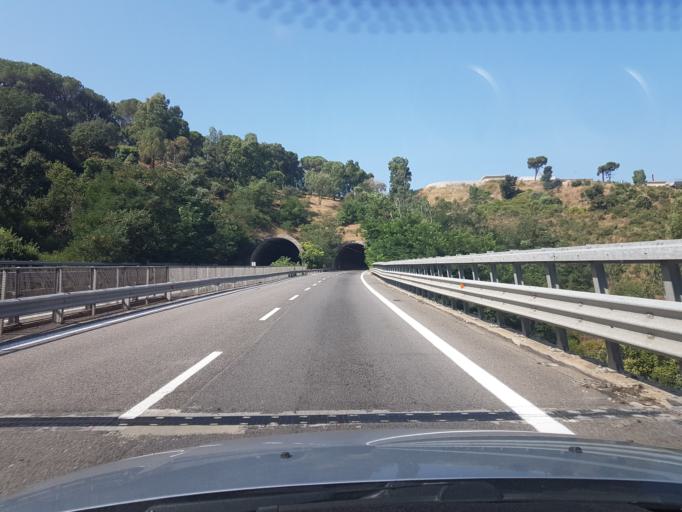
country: IT
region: Sardinia
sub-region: Provincia di Nuoro
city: Nuoro
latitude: 40.3307
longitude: 9.2917
